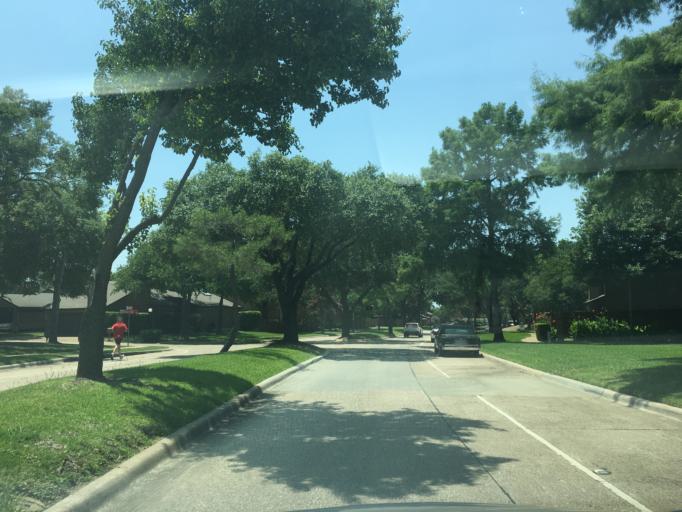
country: US
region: Texas
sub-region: Dallas County
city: Carrollton
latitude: 32.9483
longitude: -96.8684
